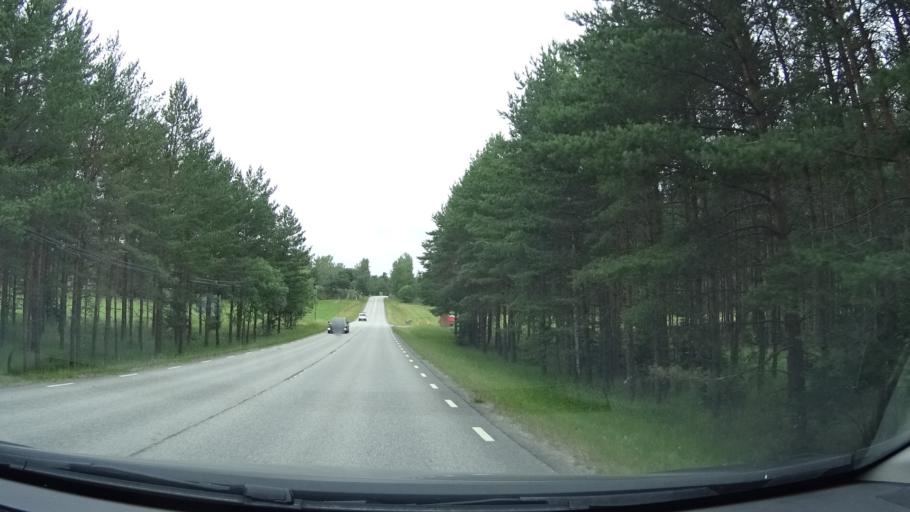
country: SE
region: Stockholm
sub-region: Varmdo Kommun
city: Hemmesta
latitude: 59.3479
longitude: 18.4788
